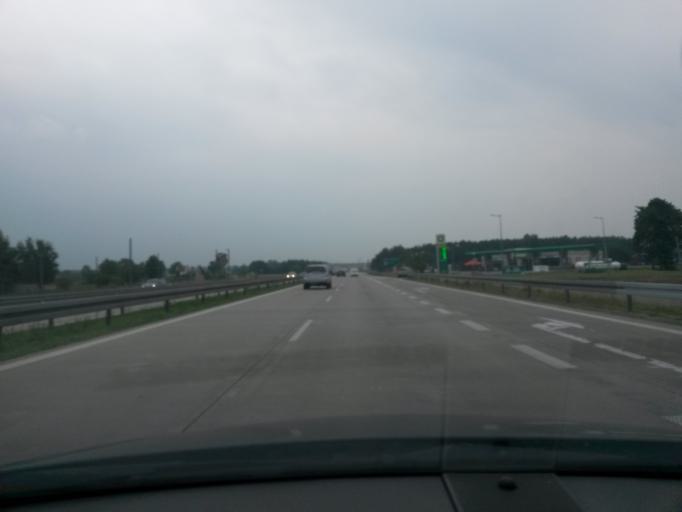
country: PL
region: Lodz Voivodeship
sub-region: Powiat piotrkowski
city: Wolborz
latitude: 51.5155
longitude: 19.9082
